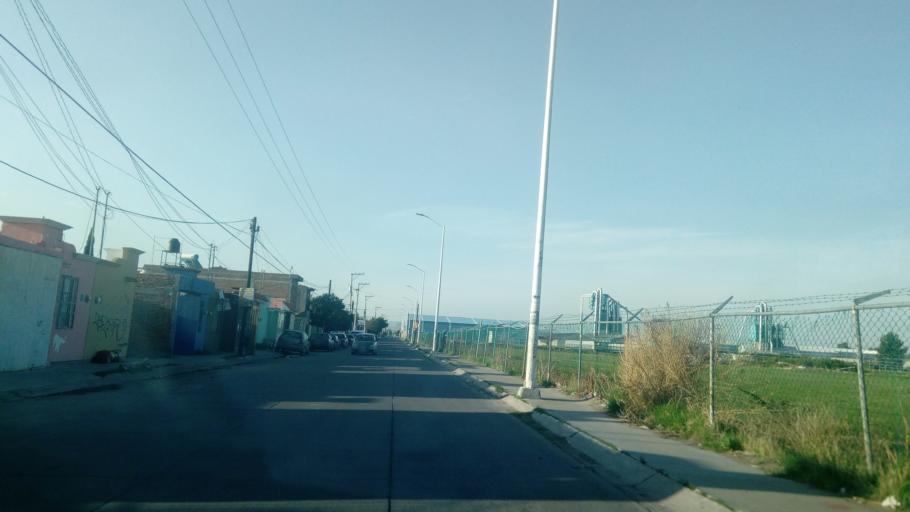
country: MX
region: Durango
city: Victoria de Durango
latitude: 24.0676
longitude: -104.5889
